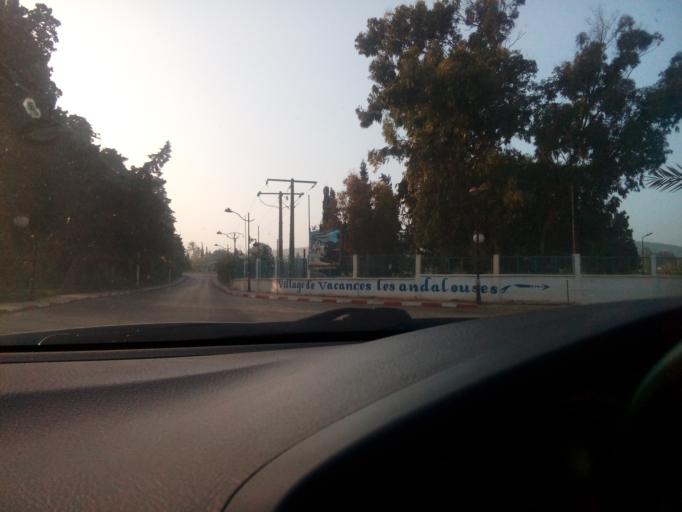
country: DZ
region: Oran
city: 'Ain el Turk
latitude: 35.7032
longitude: -0.8925
